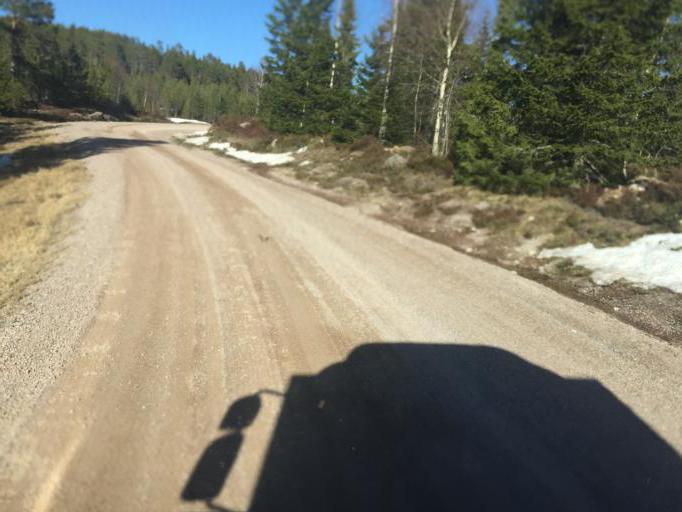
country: SE
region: Vaermland
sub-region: Filipstads Kommun
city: Lesjofors
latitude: 60.2587
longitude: 14.0029
